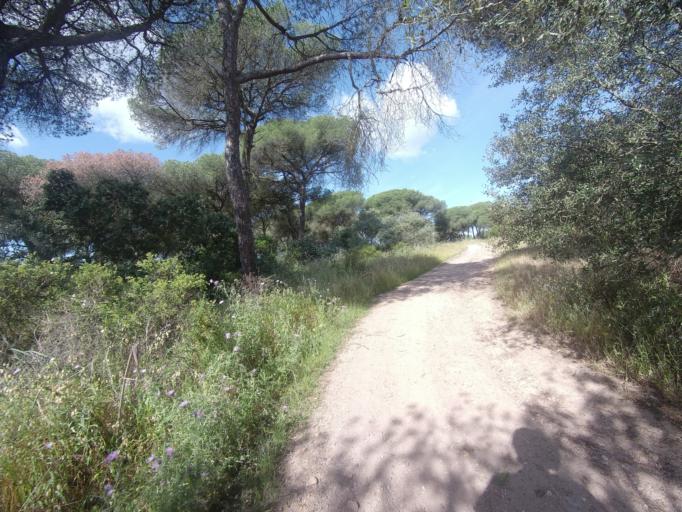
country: ES
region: Andalusia
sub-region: Provincia de Huelva
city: Aljaraque
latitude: 37.2342
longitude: -7.0357
